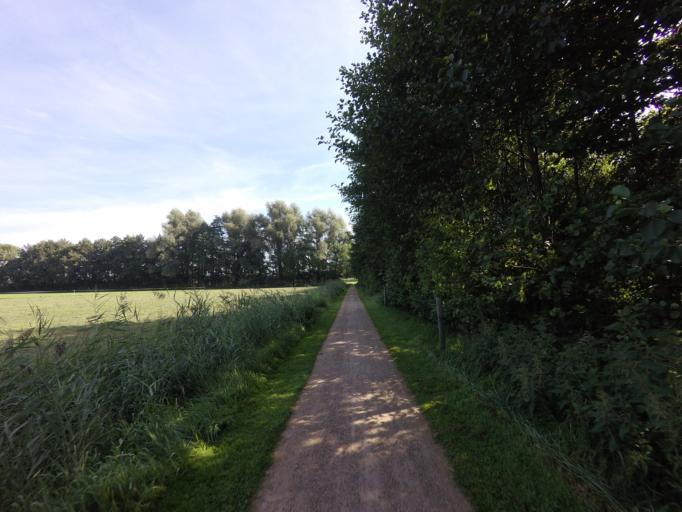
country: NL
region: Gelderland
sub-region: Oost Gelre
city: Lichtenvoorde
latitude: 52.0094
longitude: 6.5201
